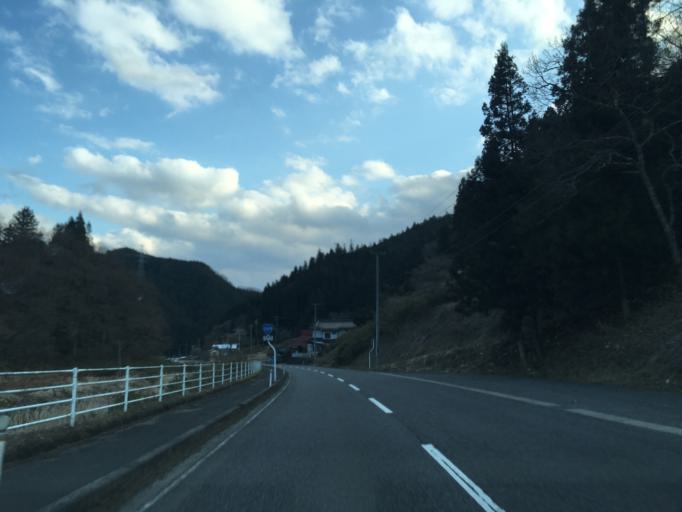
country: JP
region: Fukushima
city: Ishikawa
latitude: 37.1172
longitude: 140.5671
